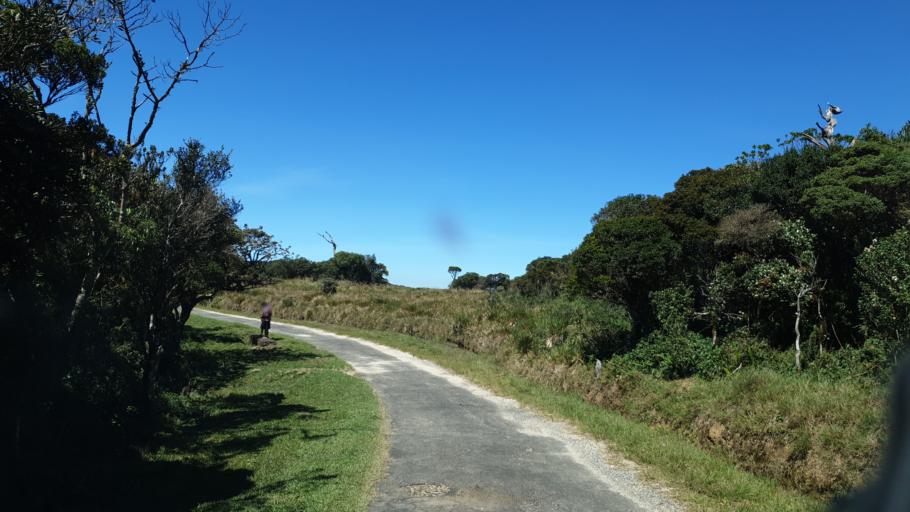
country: LK
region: Uva
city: Haputale
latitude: 6.8079
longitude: 80.8369
